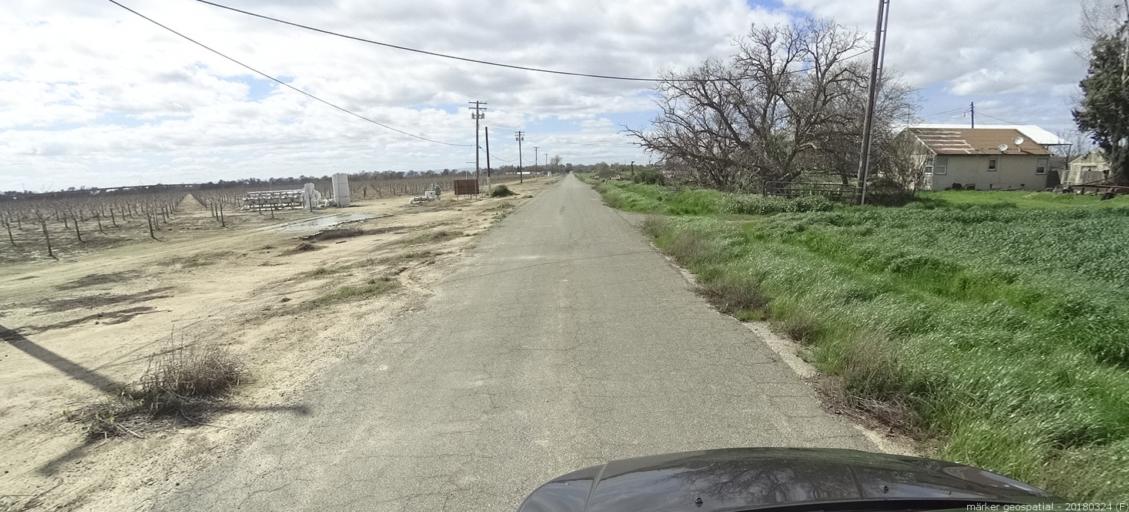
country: US
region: California
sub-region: Yolo County
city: West Sacramento
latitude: 38.6854
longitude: -121.6077
